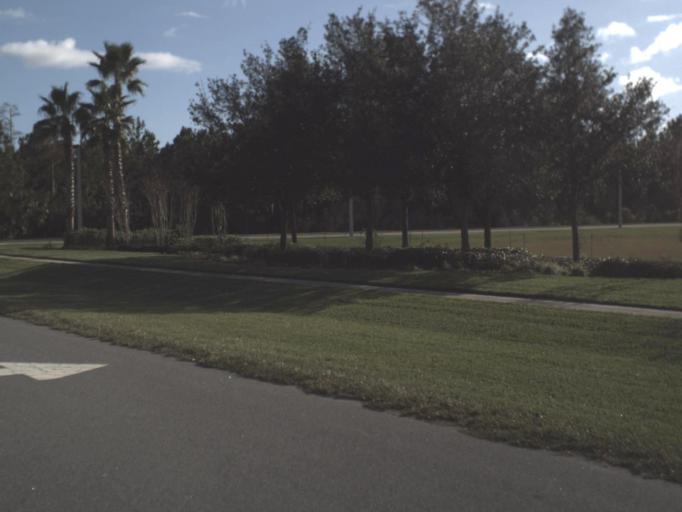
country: US
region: Florida
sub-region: Volusia County
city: Ormond Beach
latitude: 29.2463
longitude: -81.1053
